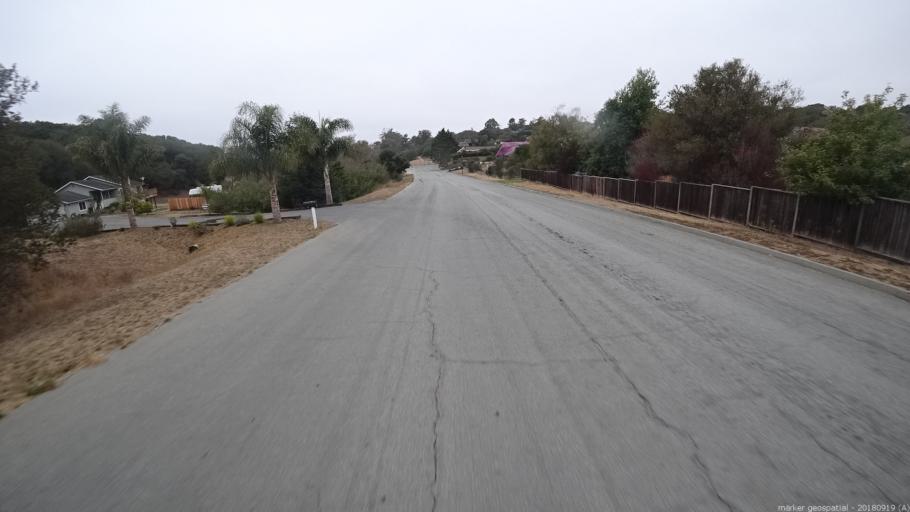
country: US
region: California
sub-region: Monterey County
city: Castroville
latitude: 36.7781
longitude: -121.7164
